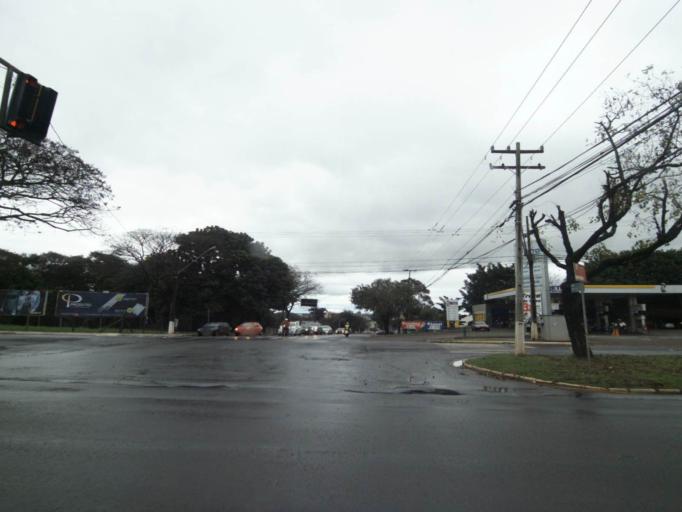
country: BR
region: Parana
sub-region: Foz Do Iguacu
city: Foz do Iguacu
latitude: -25.5170
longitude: -54.5748
